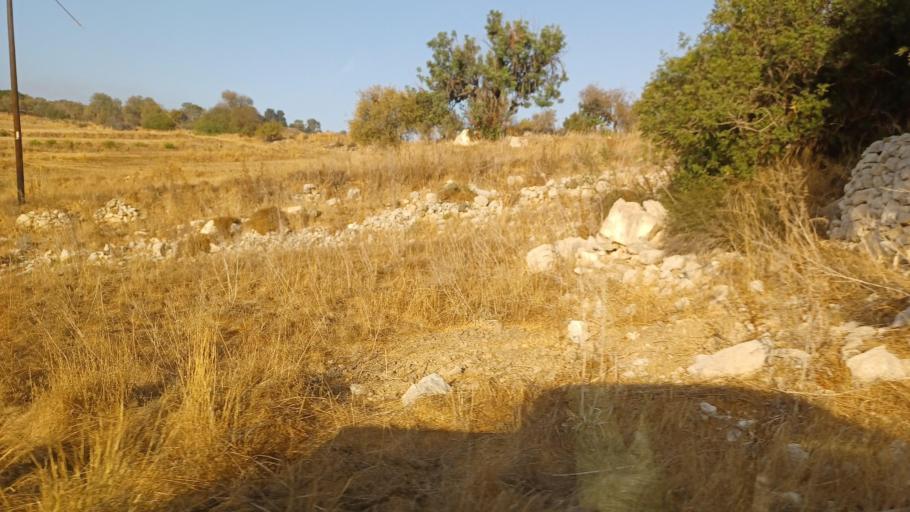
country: CY
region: Pafos
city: Polis
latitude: 34.9700
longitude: 32.4219
